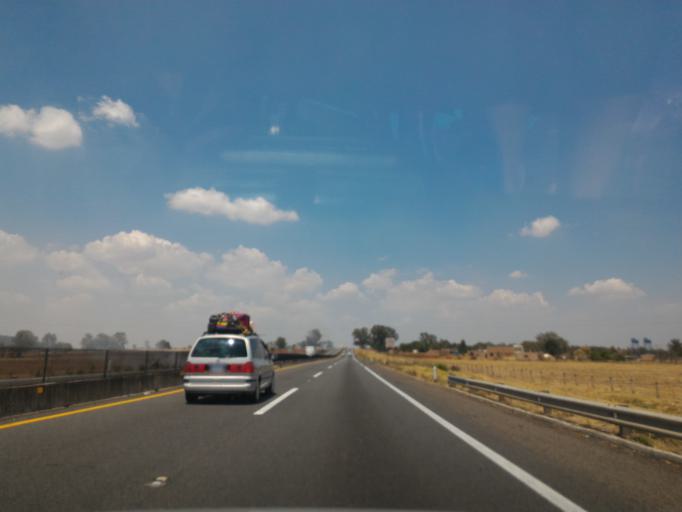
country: MX
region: Jalisco
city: Tepatitlan de Morelos
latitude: 20.8690
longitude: -102.7534
